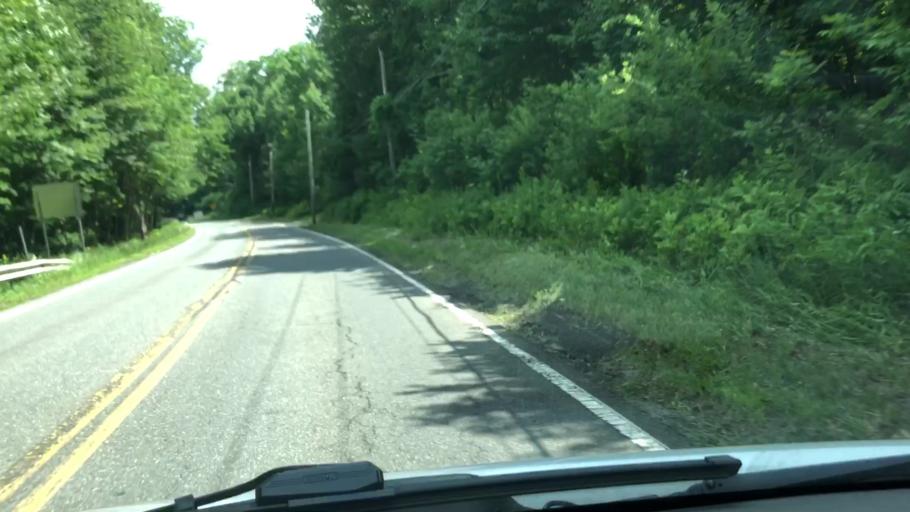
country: US
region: Massachusetts
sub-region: Hampshire County
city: Chesterfield
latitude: 42.4303
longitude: -72.7887
